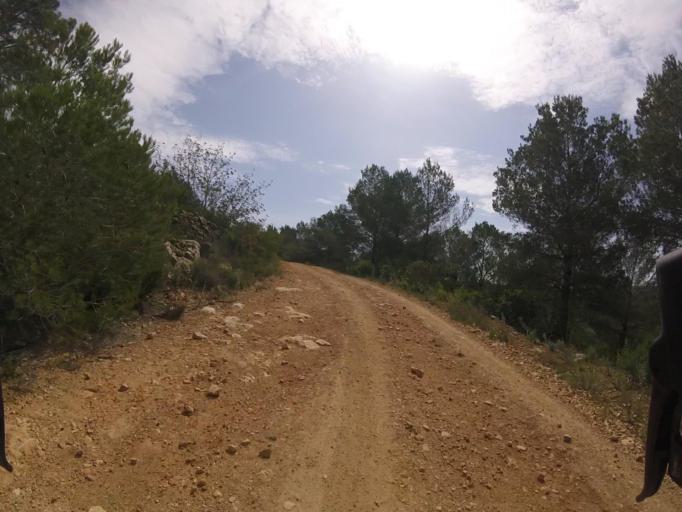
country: ES
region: Valencia
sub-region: Provincia de Castello
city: Cuevas de Vinroma
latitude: 40.2843
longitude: 0.1194
